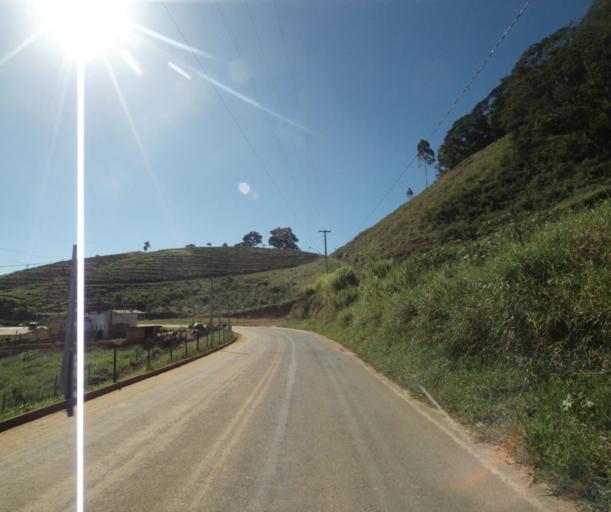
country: BR
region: Minas Gerais
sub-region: Espera Feliz
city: Espera Feliz
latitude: -20.6867
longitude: -41.8435
